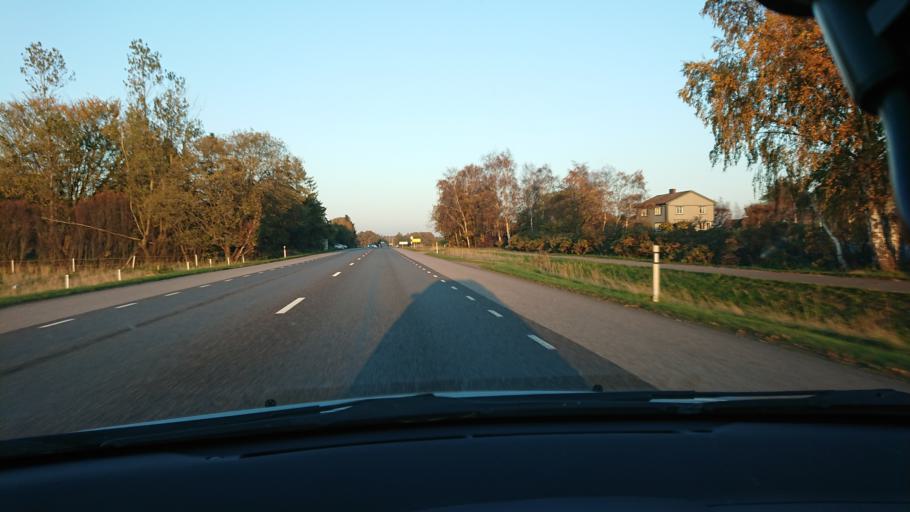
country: SE
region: Halland
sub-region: Halmstads Kommun
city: Fyllinge
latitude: 56.6900
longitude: 12.9638
